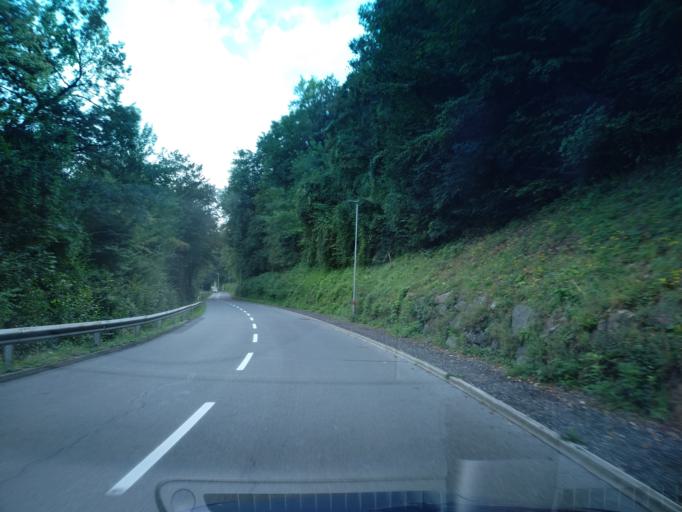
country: AT
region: Styria
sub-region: Politischer Bezirk Leibnitz
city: Leibnitz
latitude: 46.7824
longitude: 15.5261
